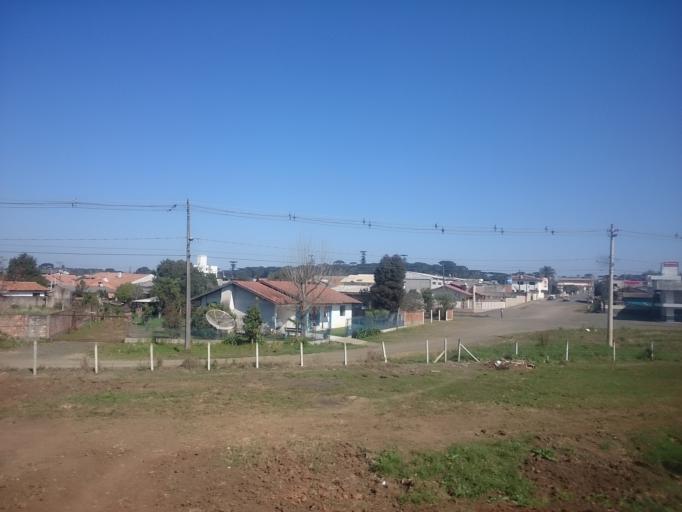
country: BR
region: Santa Catarina
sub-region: Canoinhas
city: Canoinhas
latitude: -26.3949
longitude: -50.1601
